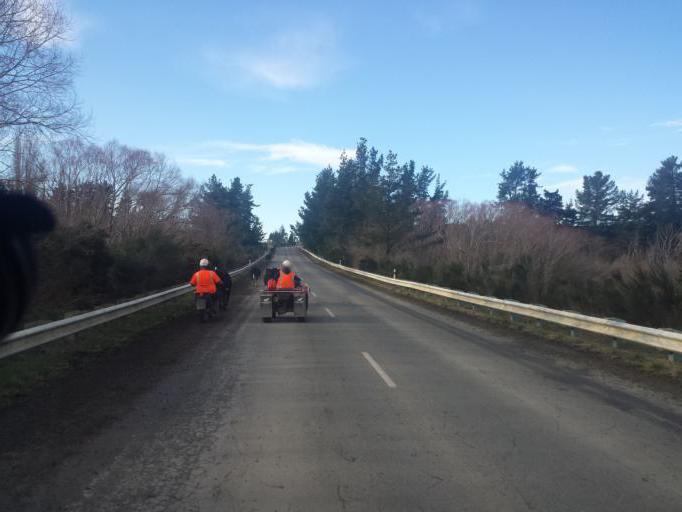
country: NZ
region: Canterbury
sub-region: Timaru District
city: Pleasant Point
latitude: -43.9733
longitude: 171.3038
